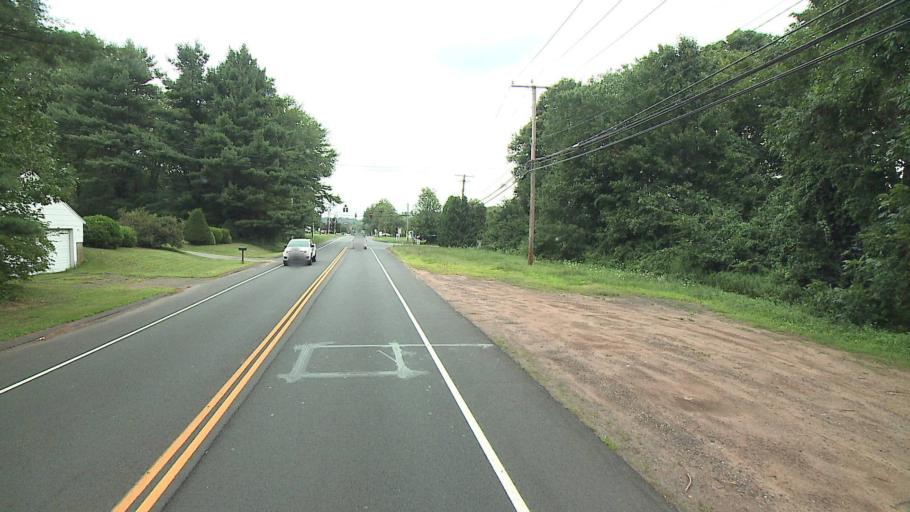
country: US
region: Connecticut
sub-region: Middlesex County
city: Cromwell
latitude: 41.6231
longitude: -72.6753
